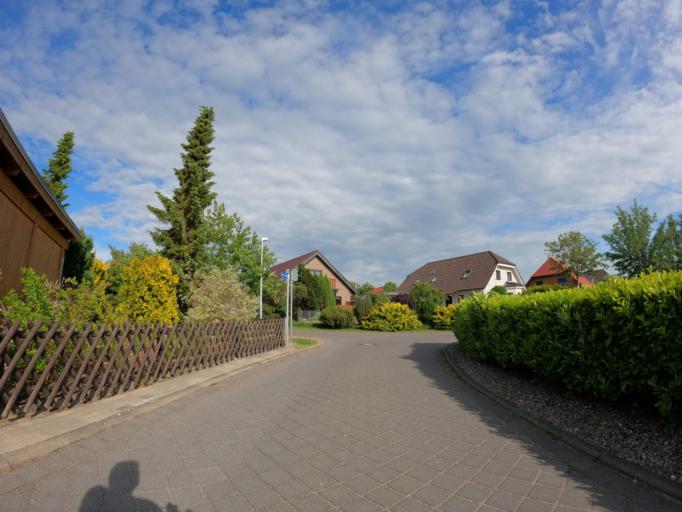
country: DE
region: Mecklenburg-Vorpommern
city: Prohn
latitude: 54.3510
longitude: 13.0129
